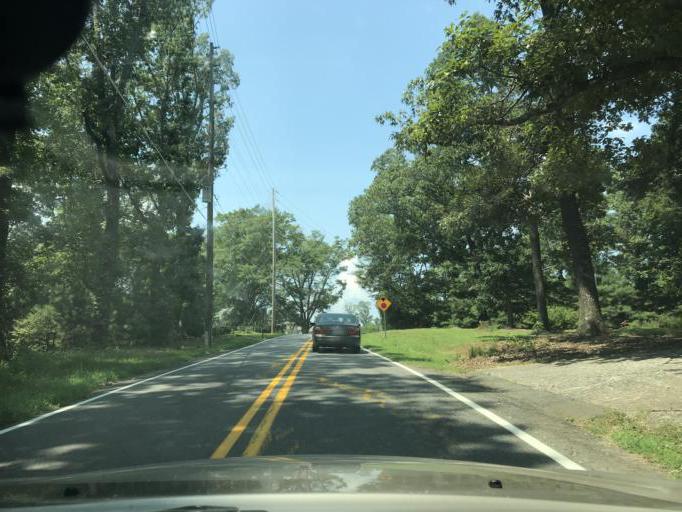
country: US
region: Georgia
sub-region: Forsyth County
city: Cumming
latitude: 34.3006
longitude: -84.0985
